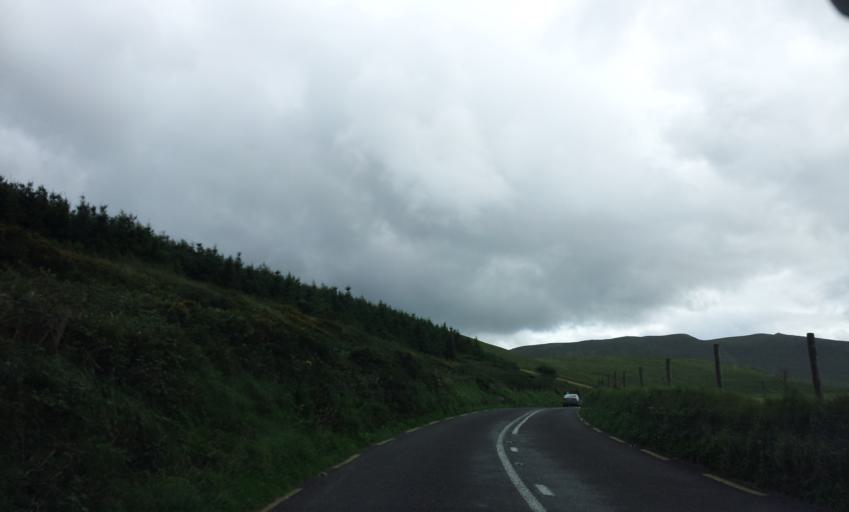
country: IE
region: Munster
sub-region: Ciarrai
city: Killorglin
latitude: 52.2091
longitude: -9.9325
